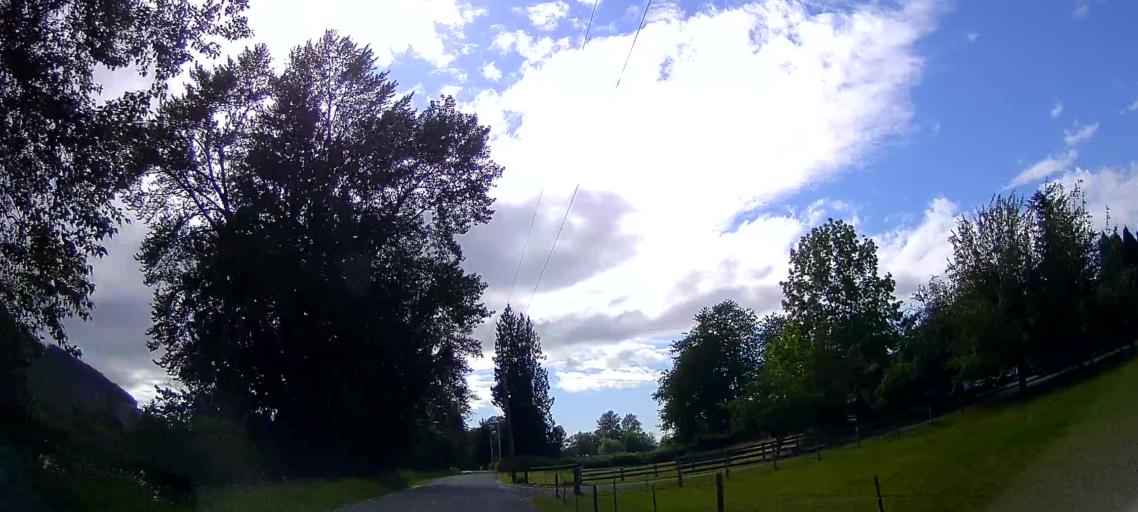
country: US
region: Washington
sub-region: Skagit County
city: Sedro-Woolley
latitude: 48.4902
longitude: -122.2133
